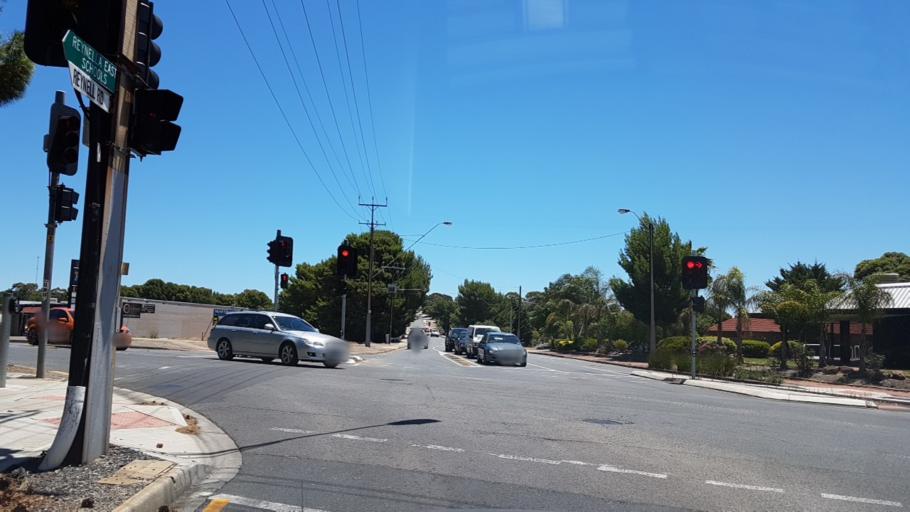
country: AU
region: South Australia
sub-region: Onkaparinga
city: Reynella
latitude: -35.0940
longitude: 138.5394
